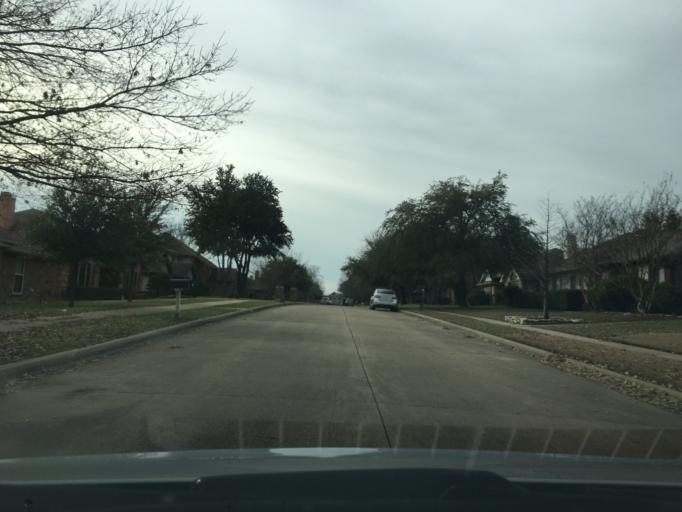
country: US
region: Texas
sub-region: Collin County
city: McKinney
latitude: 33.1938
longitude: -96.6428
